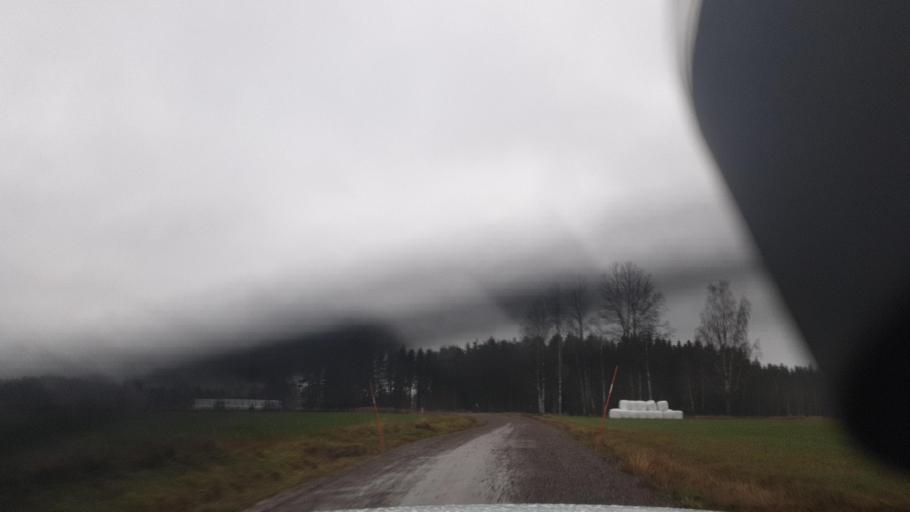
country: SE
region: Vaermland
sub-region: Eda Kommun
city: Charlottenberg
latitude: 59.7375
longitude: 12.1478
